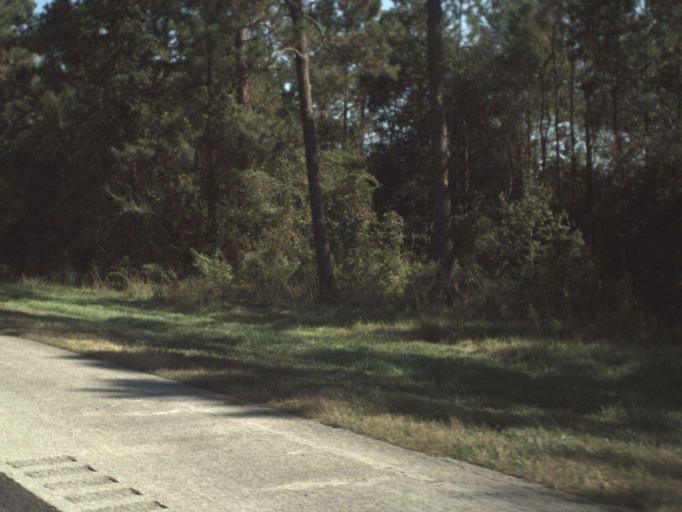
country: US
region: Florida
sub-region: Holmes County
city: Bonifay
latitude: 30.7603
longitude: -85.7624
